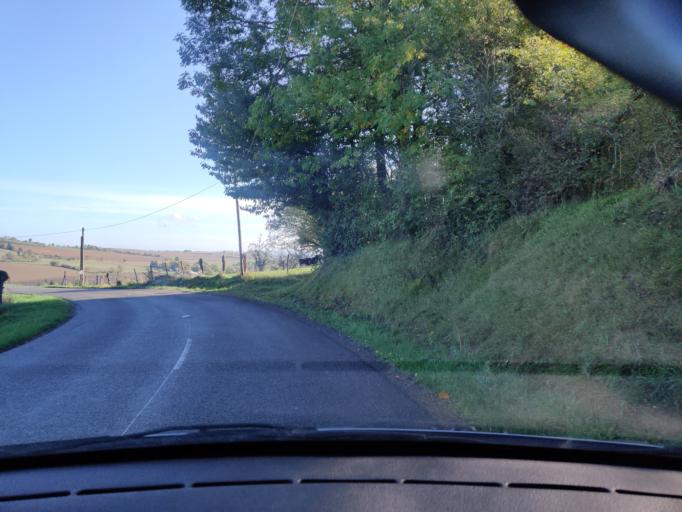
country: FR
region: Auvergne
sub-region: Departement du Puy-de-Dome
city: Aigueperse
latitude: 46.0281
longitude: 3.1754
